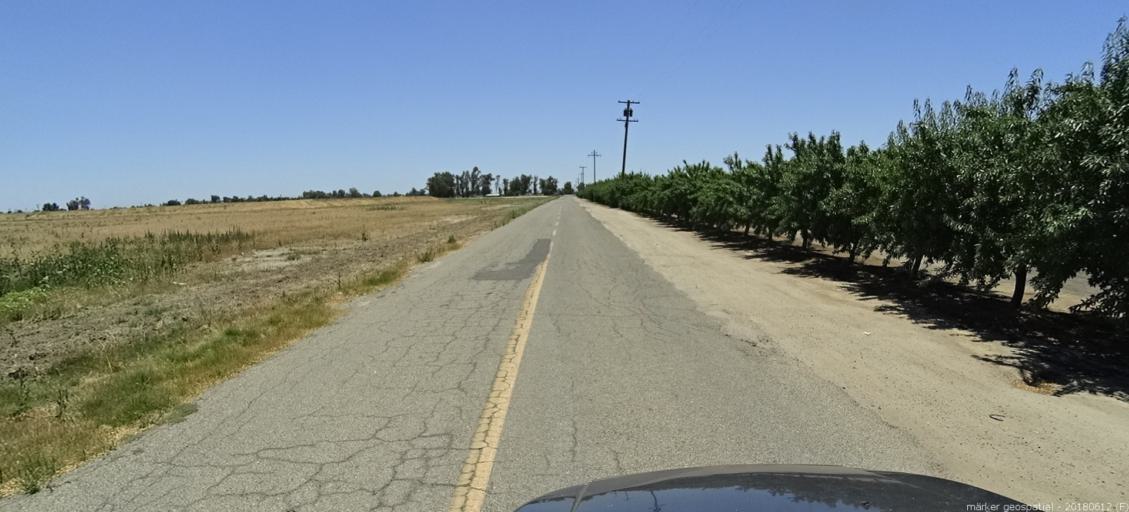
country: US
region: California
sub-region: Madera County
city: Chowchilla
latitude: 37.1053
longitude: -120.2658
